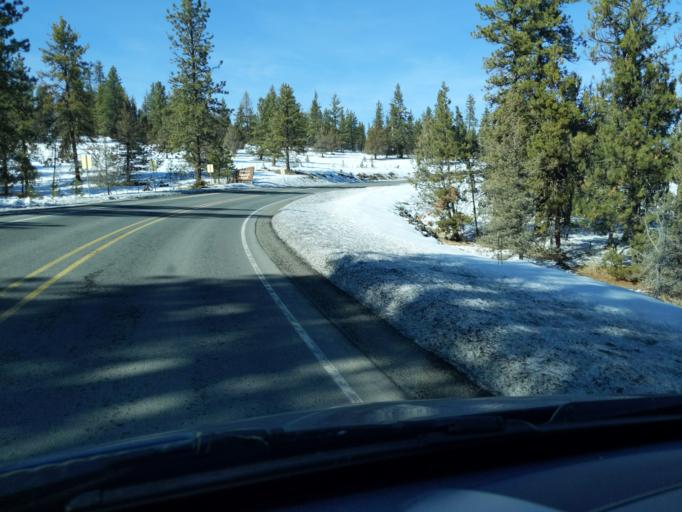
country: US
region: Oregon
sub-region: Grant County
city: John Day
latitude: 44.9104
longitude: -119.0104
